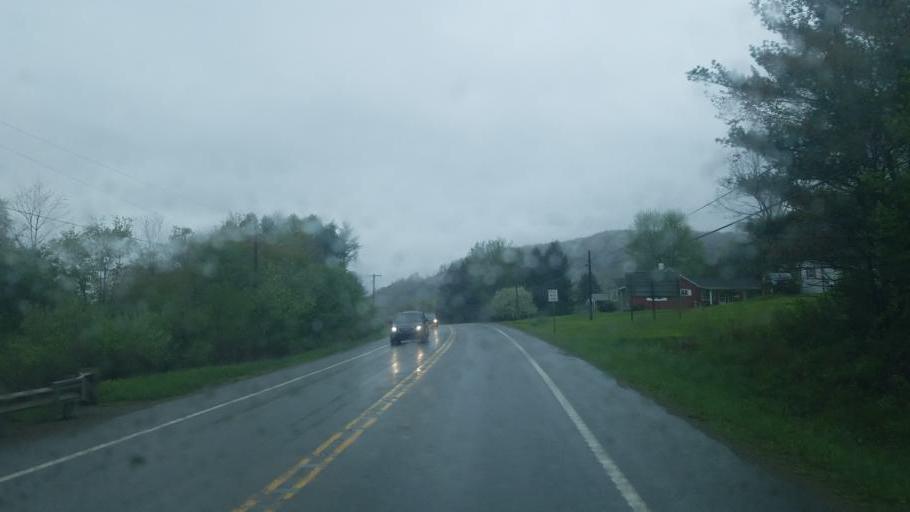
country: US
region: Pennsylvania
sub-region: Potter County
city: Coudersport
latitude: 41.7577
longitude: -78.1106
